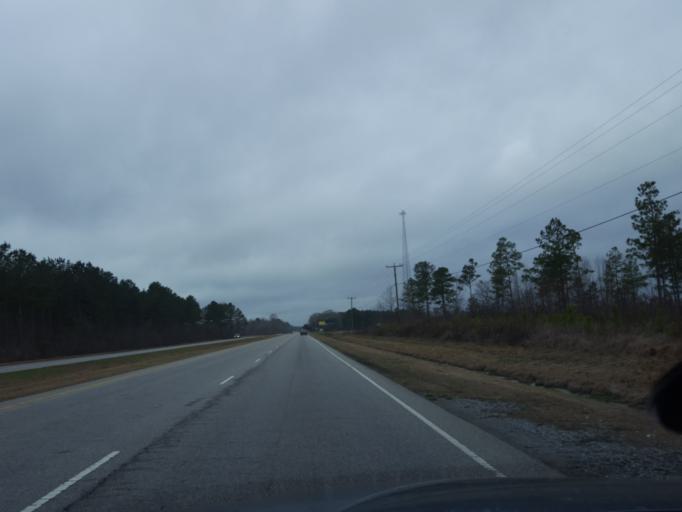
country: US
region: North Carolina
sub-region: Washington County
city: Plymouth
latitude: 35.8117
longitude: -76.8561
